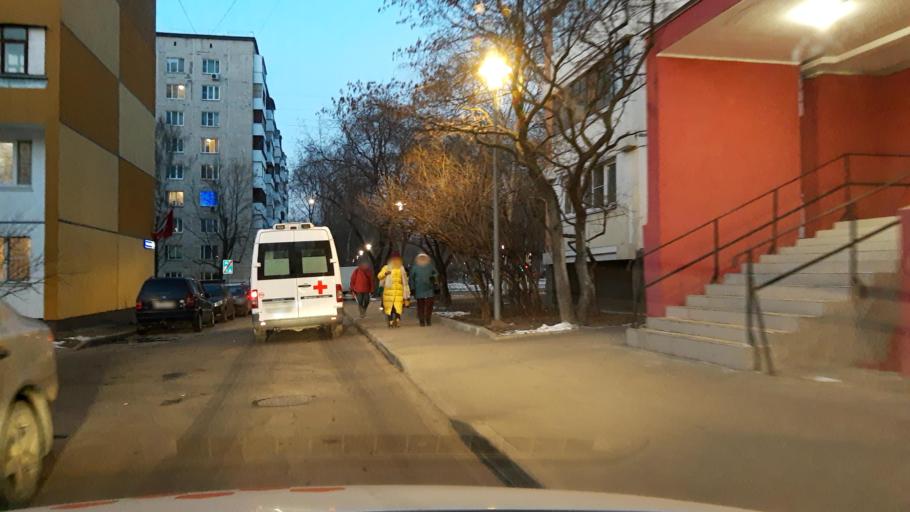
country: RU
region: Moskovskaya
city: Alekseyevka
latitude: 55.6332
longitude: 37.7985
